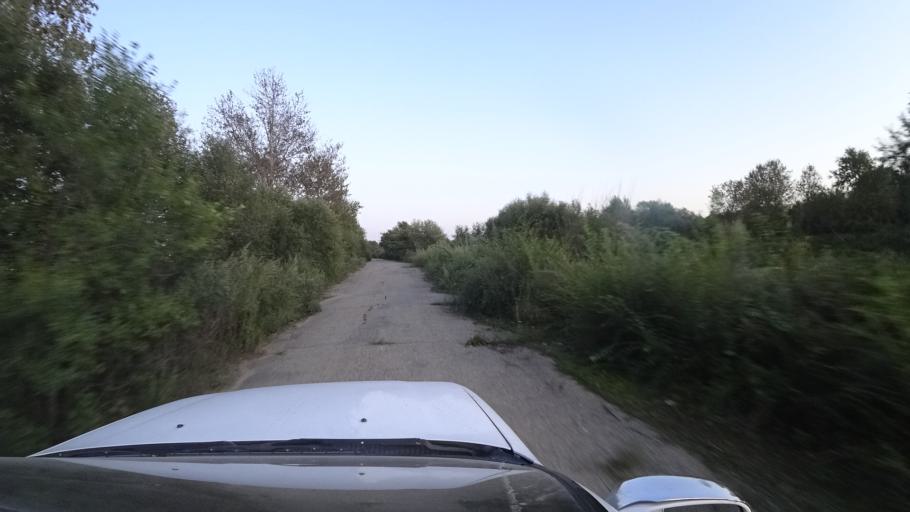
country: RU
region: Primorskiy
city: Dal'nerechensk
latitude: 45.9481
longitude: 133.7625
